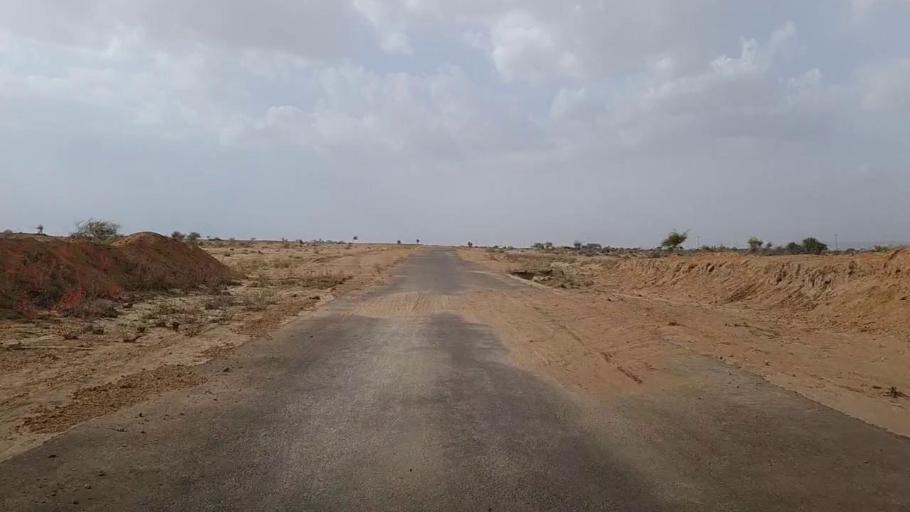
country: PK
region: Sindh
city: Jamshoro
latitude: 25.4631
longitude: 67.6773
